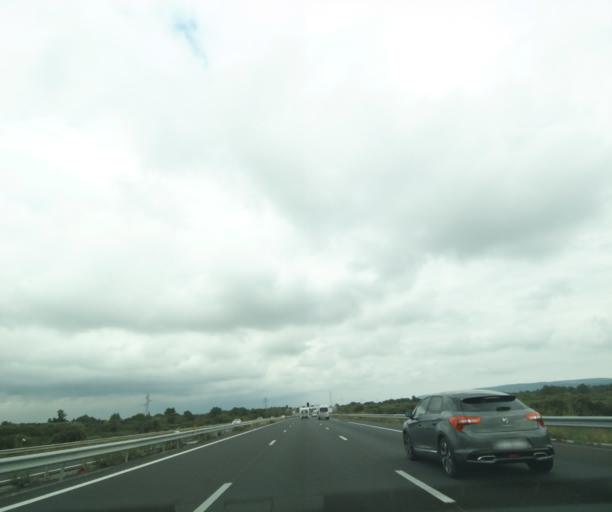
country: FR
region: Languedoc-Roussillon
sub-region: Departement de l'Herault
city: Bouzigues
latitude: 43.4718
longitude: 3.6441
